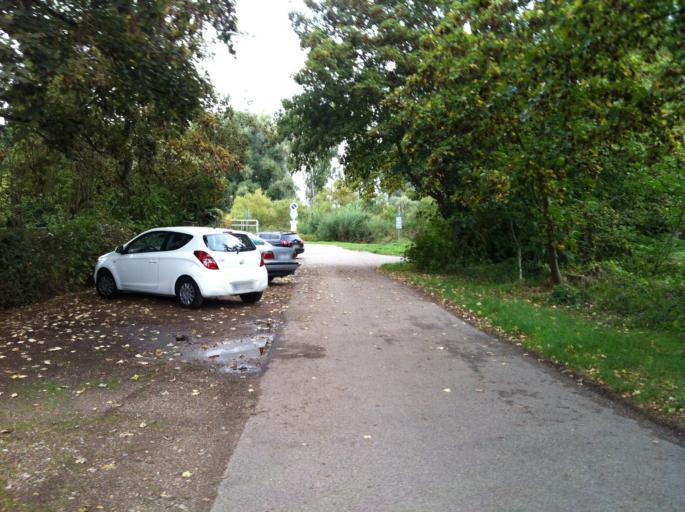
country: DE
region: Rheinland-Pfalz
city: Budenheim
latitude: 50.0318
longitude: 8.1999
